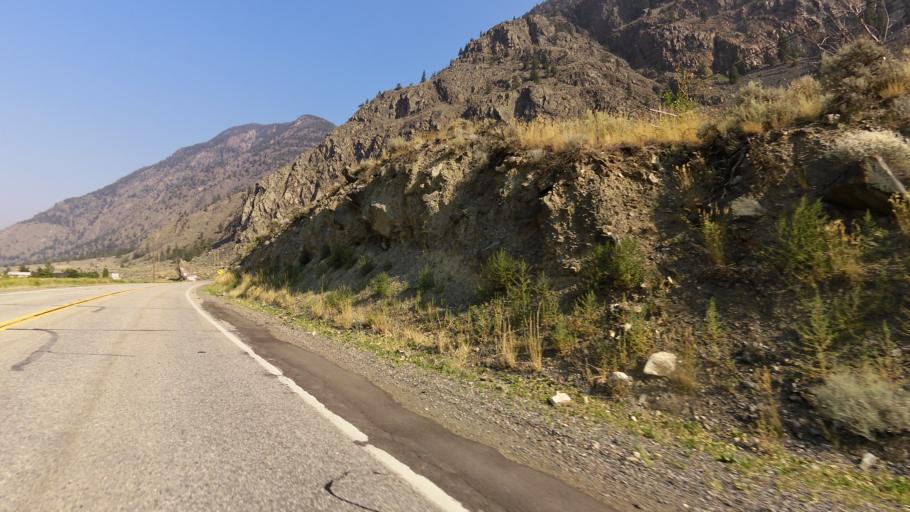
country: CA
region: British Columbia
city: Oliver
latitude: 49.2156
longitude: -119.9113
